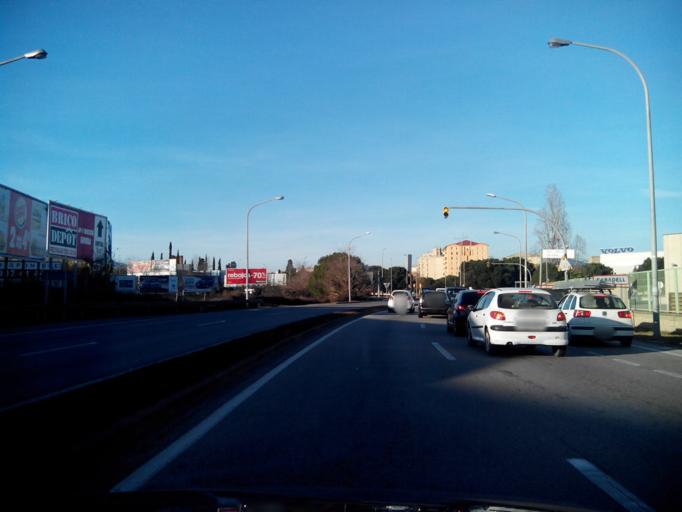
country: ES
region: Catalonia
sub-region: Provincia de Barcelona
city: Sant Quirze del Valles
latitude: 41.5351
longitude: 2.0957
